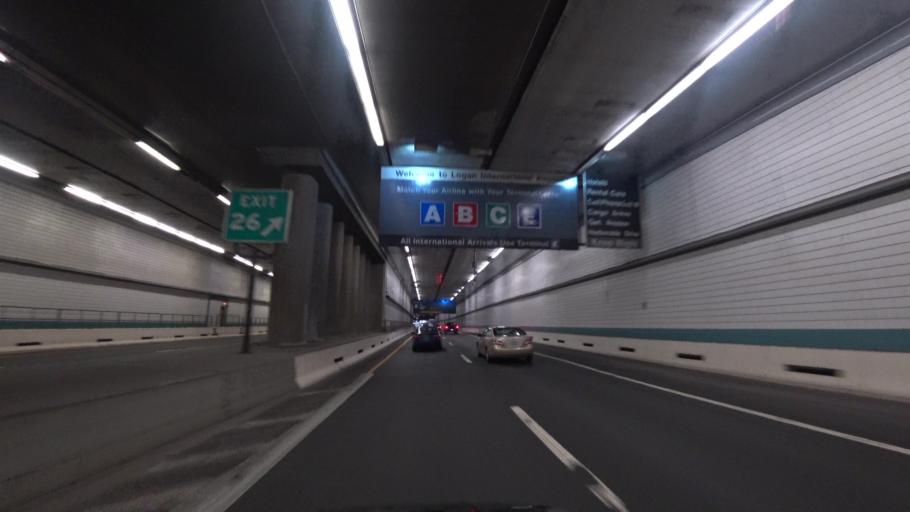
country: US
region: Massachusetts
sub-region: Suffolk County
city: Chelsea
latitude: 42.3613
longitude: -71.0269
